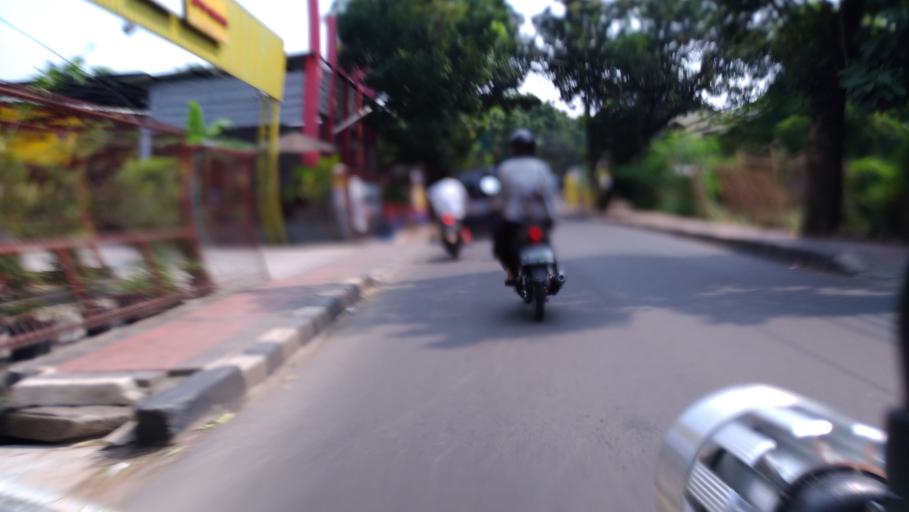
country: ID
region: West Java
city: Cileungsir
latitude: -6.3522
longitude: 106.8897
